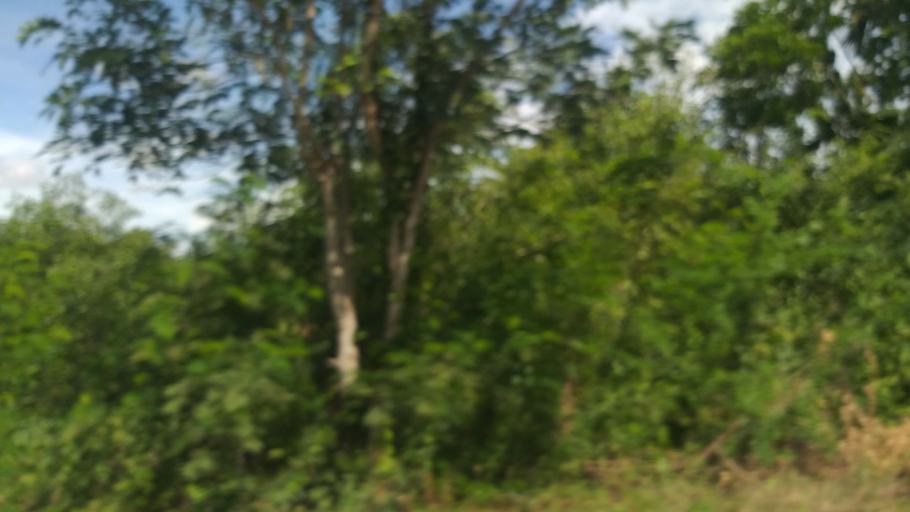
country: TH
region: Khon Kaen
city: Nong Ruea
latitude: 16.4628
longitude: 102.4417
